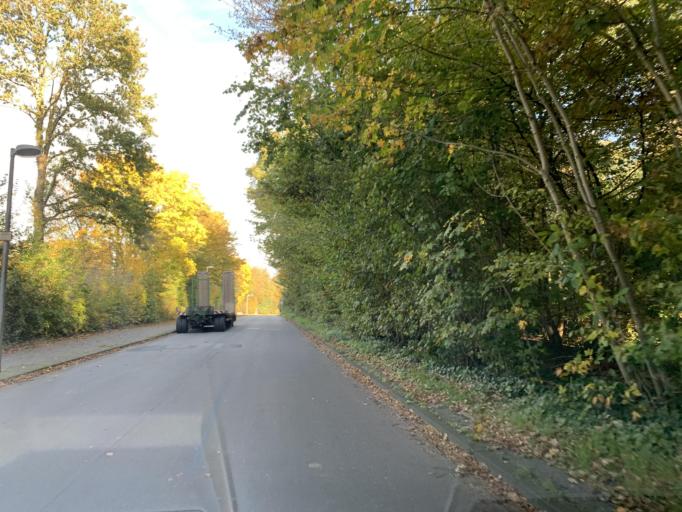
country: DE
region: North Rhine-Westphalia
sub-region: Regierungsbezirk Munster
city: Muenster
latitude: 51.9771
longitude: 7.5757
